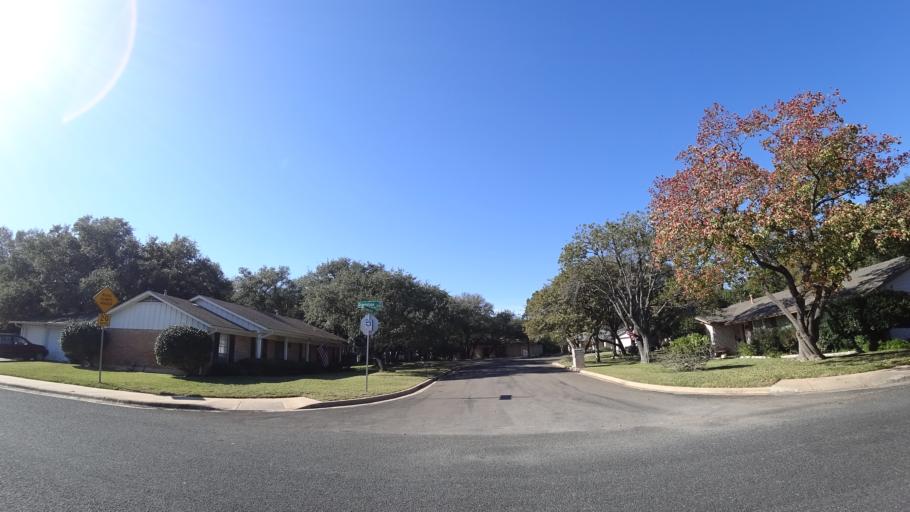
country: US
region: Texas
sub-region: Williamson County
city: Jollyville
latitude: 30.3712
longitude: -97.7504
